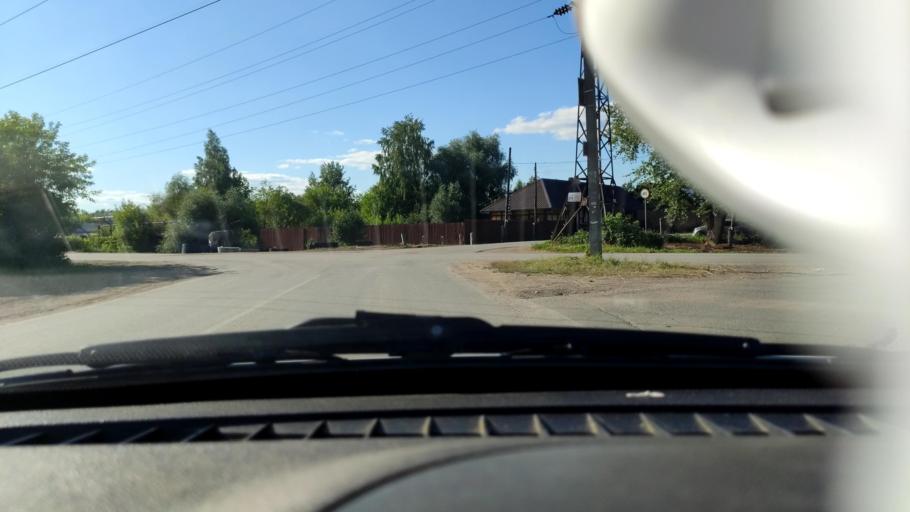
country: RU
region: Perm
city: Krasnokamsk
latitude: 58.0742
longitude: 55.7970
